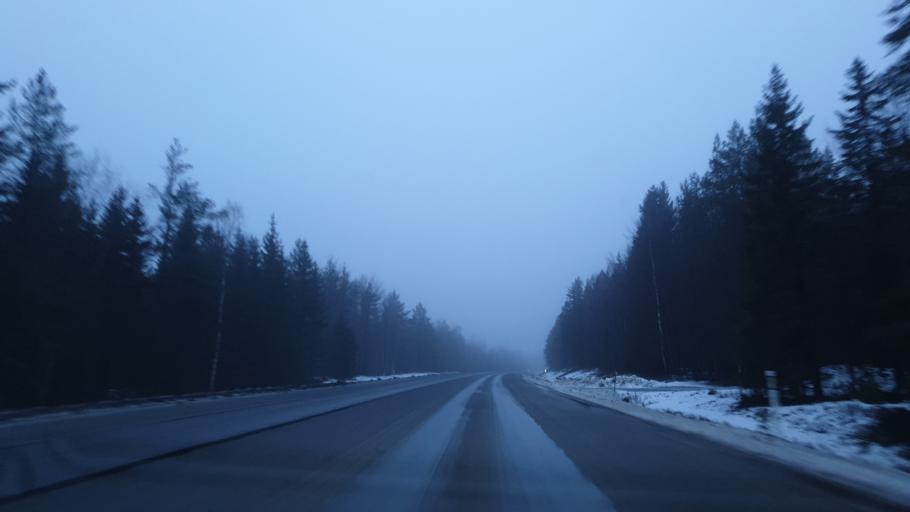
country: SE
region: Vaesterbotten
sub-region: Umea Kommun
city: Holmsund
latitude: 63.7608
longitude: 20.3452
